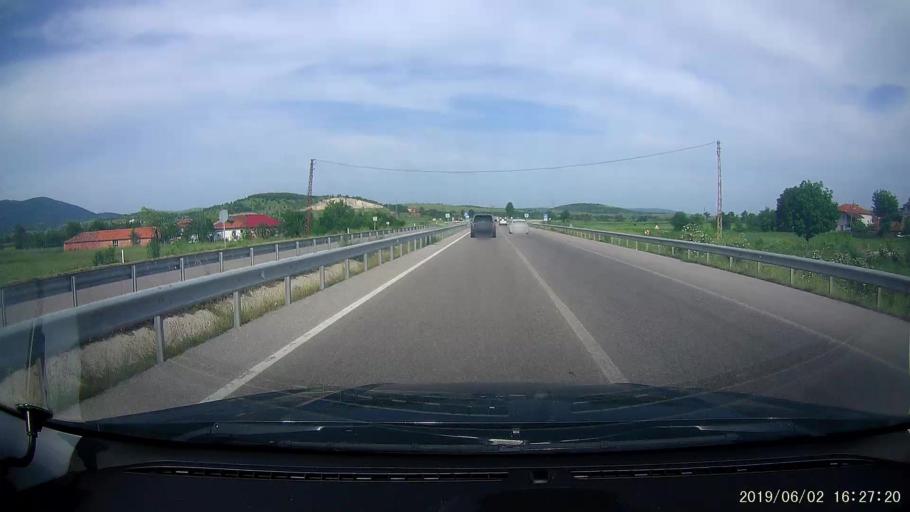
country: TR
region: Samsun
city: Ladik
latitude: 41.0019
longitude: 35.8250
